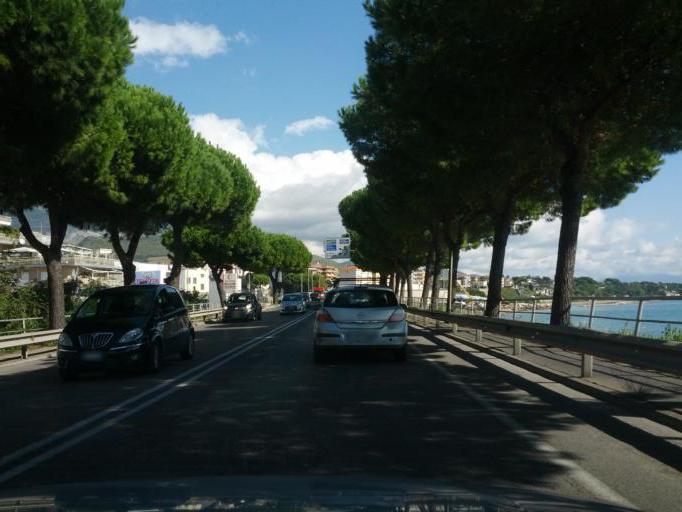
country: IT
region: Latium
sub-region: Provincia di Latina
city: Formia
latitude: 41.2589
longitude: 13.6156
